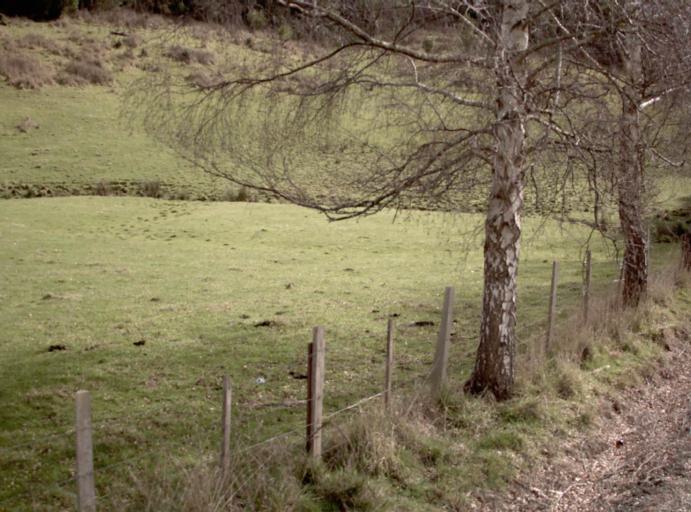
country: AU
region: Tasmania
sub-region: Launceston
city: Mayfield
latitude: -41.2501
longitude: 147.2456
